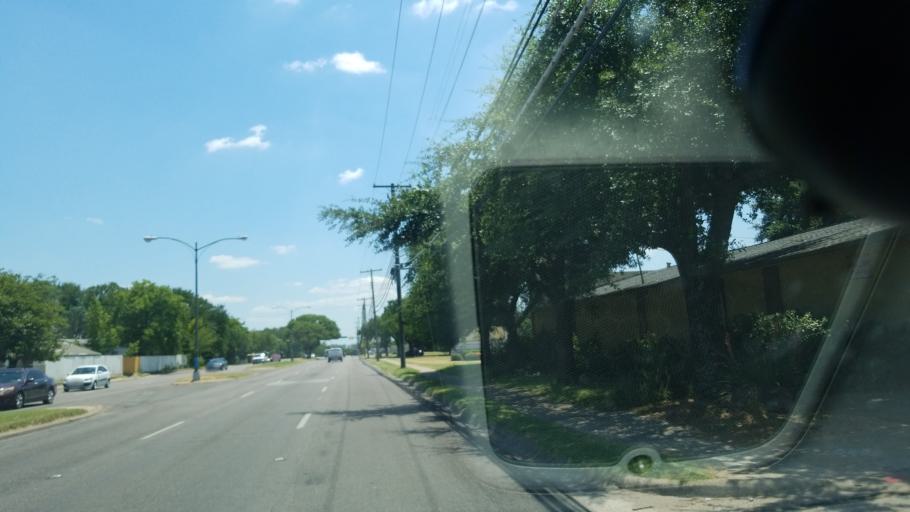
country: US
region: Texas
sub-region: Dallas County
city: Cockrell Hill
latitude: 32.7163
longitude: -96.8571
